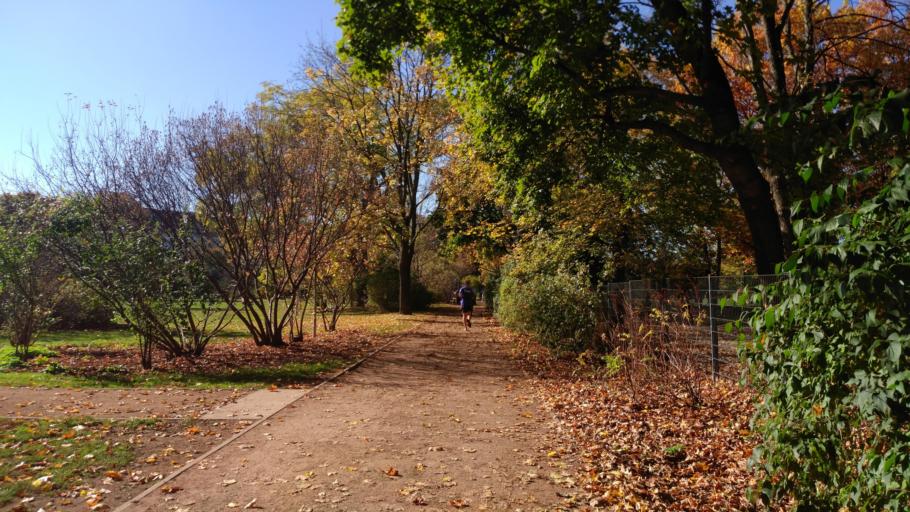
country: DE
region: Saxony
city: Albertstadt
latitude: 51.0702
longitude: 13.7595
